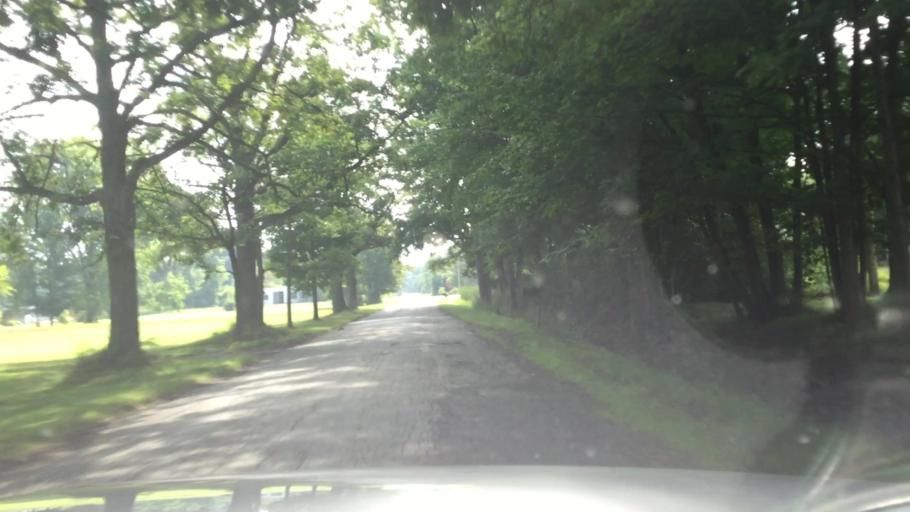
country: US
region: Michigan
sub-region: Genesee County
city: Clio
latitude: 43.2213
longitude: -83.6989
